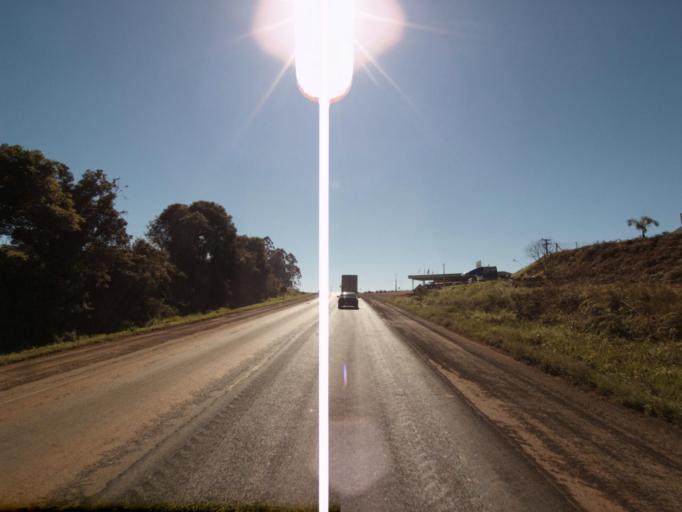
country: BR
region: Rio Grande do Sul
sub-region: Frederico Westphalen
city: Frederico Westphalen
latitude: -26.9082
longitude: -53.1873
